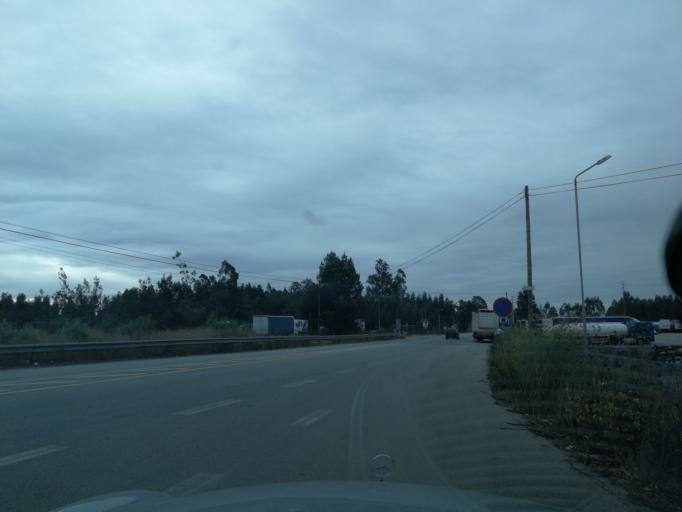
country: PT
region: Aveiro
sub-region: Albergaria-A-Velha
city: Albergaria-a-Velha
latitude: 40.6721
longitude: -8.4736
